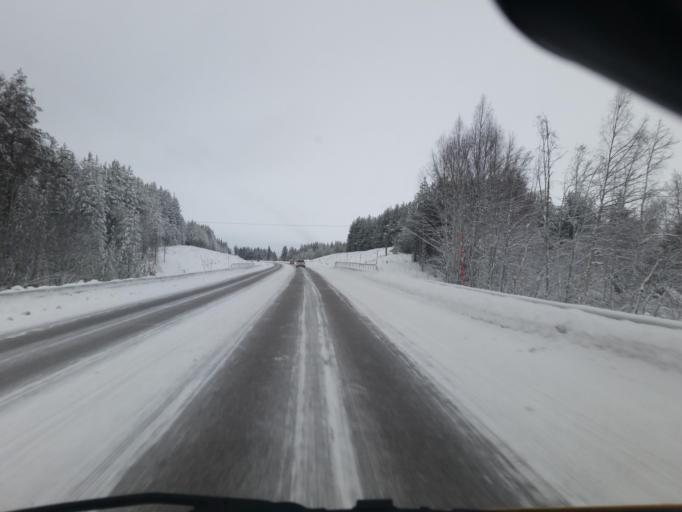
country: SE
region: Norrbotten
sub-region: Pitea Kommun
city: Bergsviken
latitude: 65.3170
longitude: 21.3853
